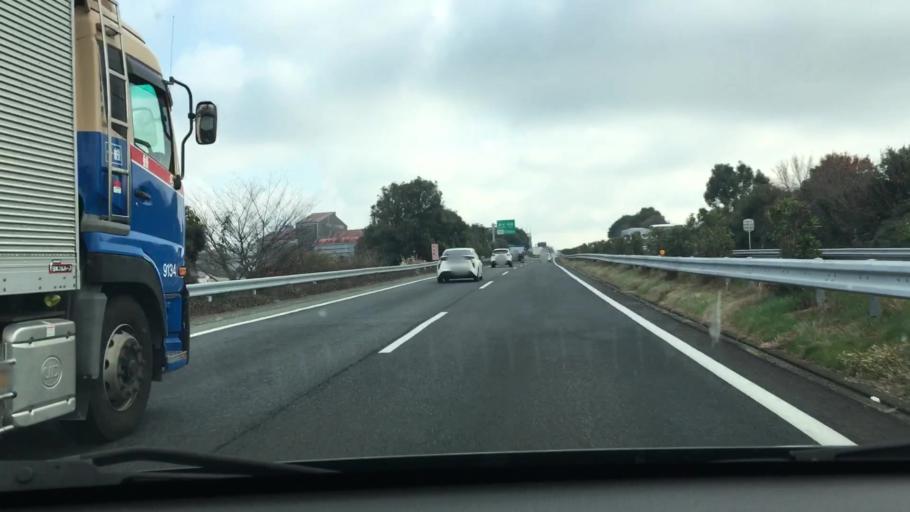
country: JP
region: Kumamoto
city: Kumamoto
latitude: 32.8419
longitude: 130.7740
